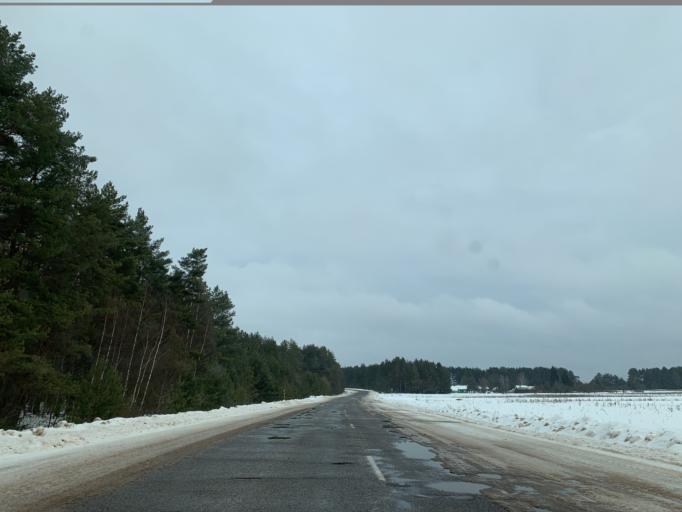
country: BY
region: Minsk
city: Il'ya
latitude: 54.3260
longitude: 27.2491
